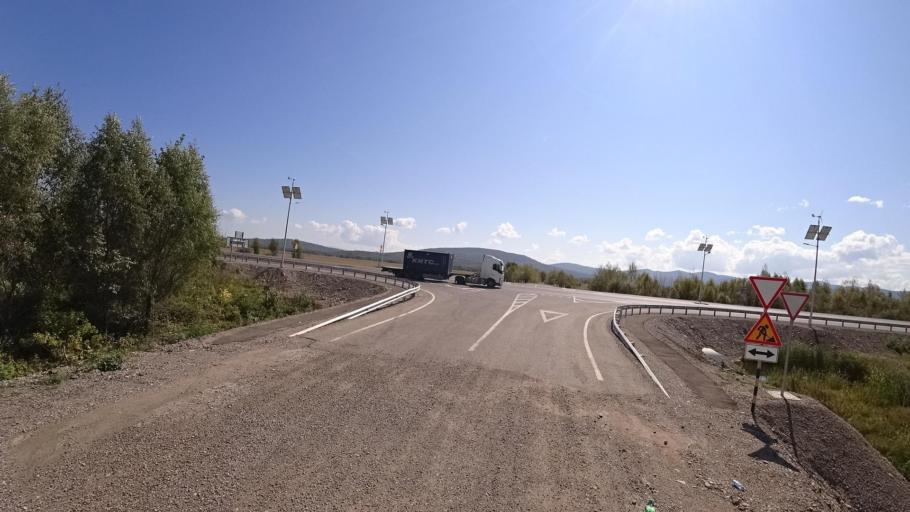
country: RU
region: Jewish Autonomous Oblast
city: Londoko
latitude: 49.0029
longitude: 131.9454
